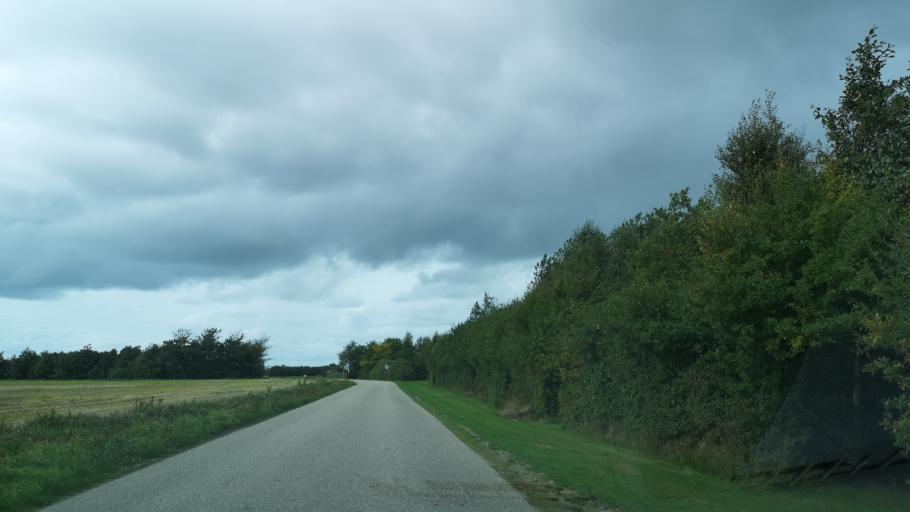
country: DK
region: South Denmark
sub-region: Varde Kommune
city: Oksbol
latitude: 55.8357
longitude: 8.3101
